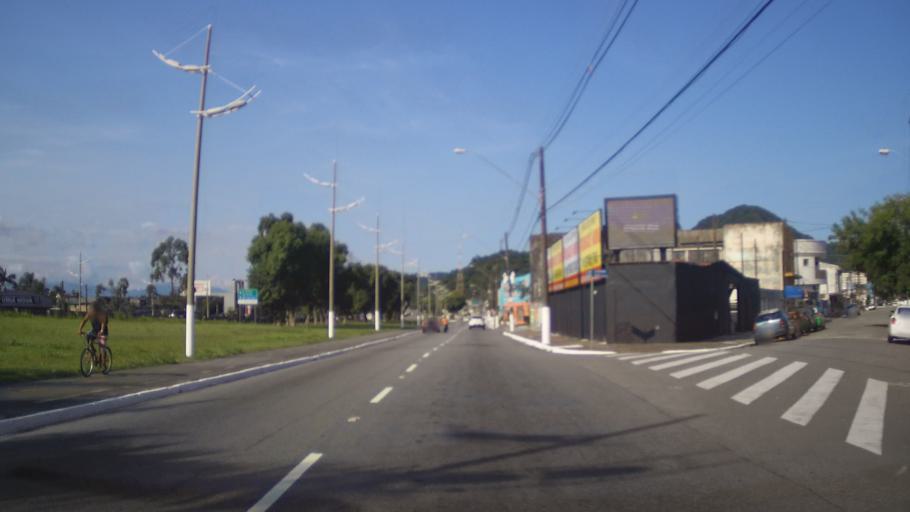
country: BR
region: Sao Paulo
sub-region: Praia Grande
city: Praia Grande
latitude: -24.0024
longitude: -46.4201
